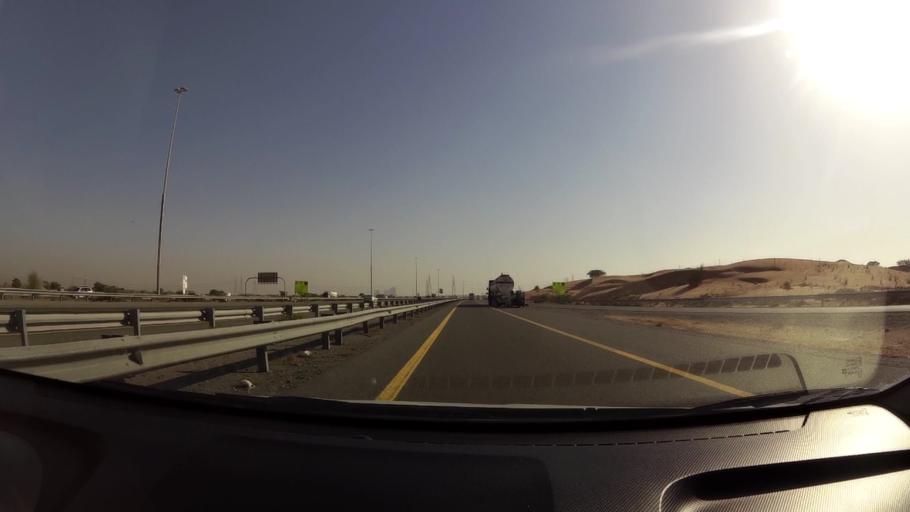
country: AE
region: Umm al Qaywayn
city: Umm al Qaywayn
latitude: 25.4478
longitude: 55.6105
